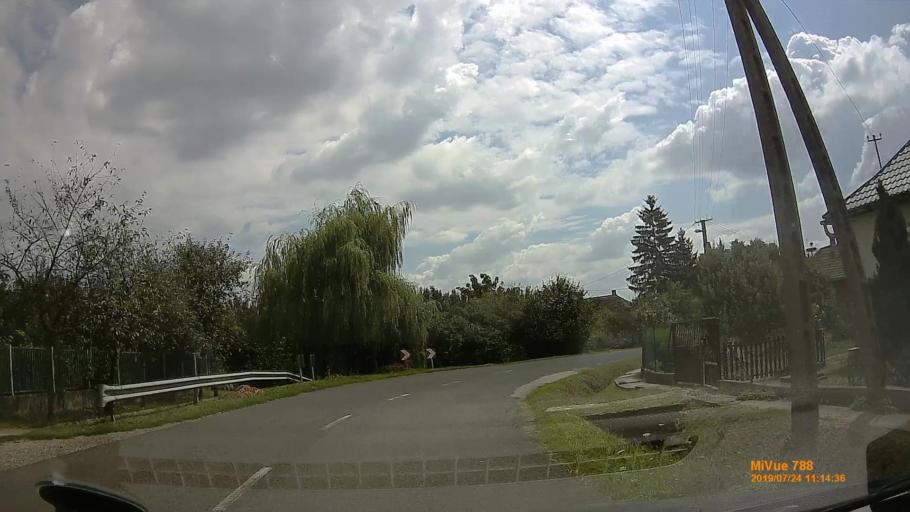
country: HU
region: Szabolcs-Szatmar-Bereg
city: Tarpa
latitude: 48.1967
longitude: 22.4504
